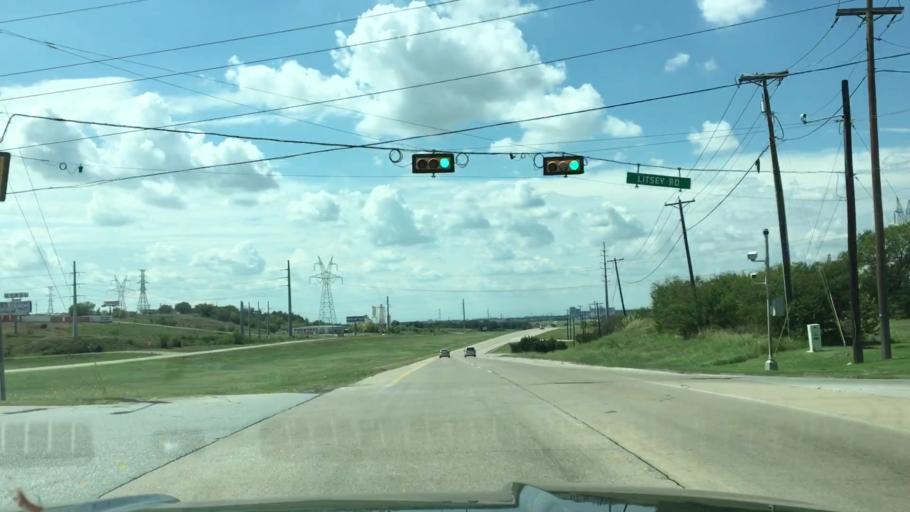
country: US
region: Texas
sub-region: Denton County
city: Roanoke
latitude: 33.0162
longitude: -97.2347
